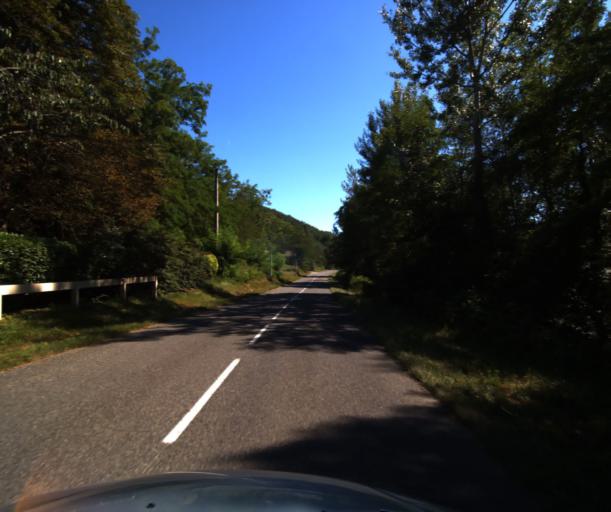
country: FR
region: Midi-Pyrenees
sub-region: Departement de la Haute-Garonne
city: Eaunes
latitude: 43.4358
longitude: 1.3265
